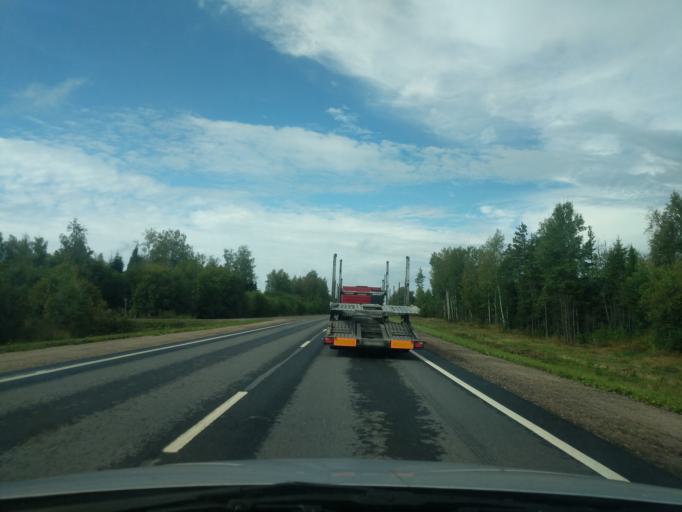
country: RU
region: Kostroma
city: Sudislavl'
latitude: 57.8237
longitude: 41.8984
